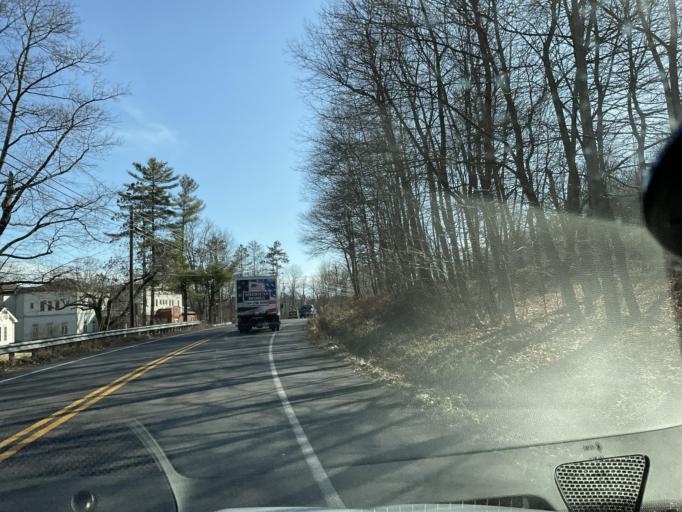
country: US
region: Maryland
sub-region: Garrett County
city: Oakland
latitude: 39.4100
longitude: -79.4119
